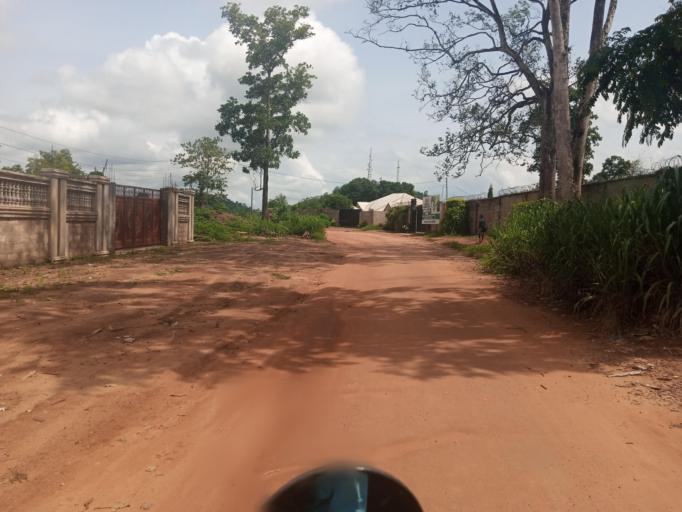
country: SL
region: Southern Province
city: Bo
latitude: 7.9683
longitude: -11.7493
